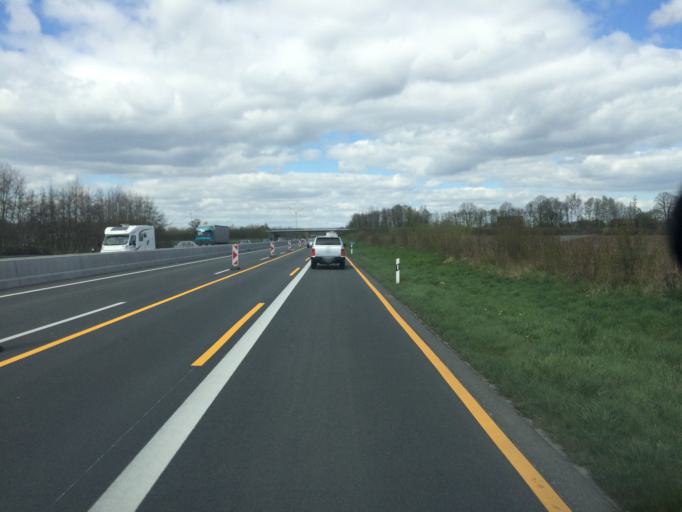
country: DE
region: North Rhine-Westphalia
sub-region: Regierungsbezirk Munster
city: Gescher
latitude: 51.9520
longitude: 7.0462
